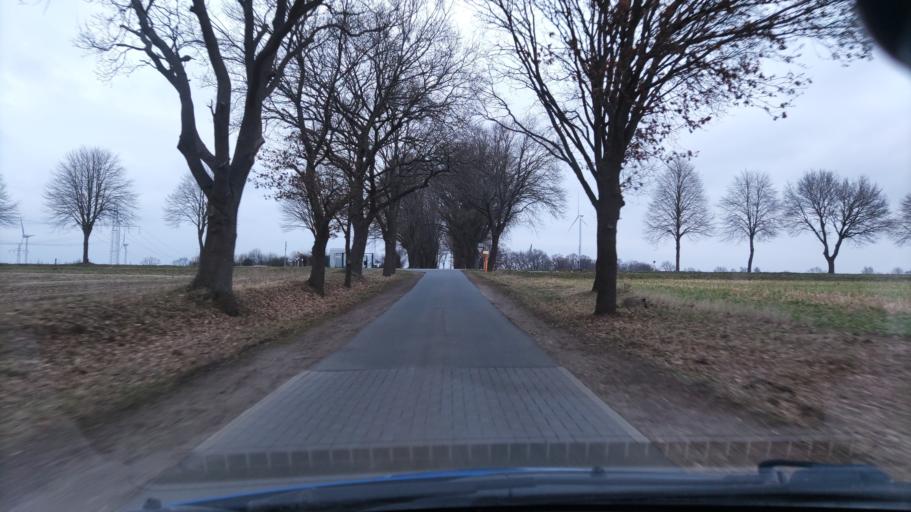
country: DE
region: Lower Saxony
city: Melbeck
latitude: 53.1806
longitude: 10.3888
